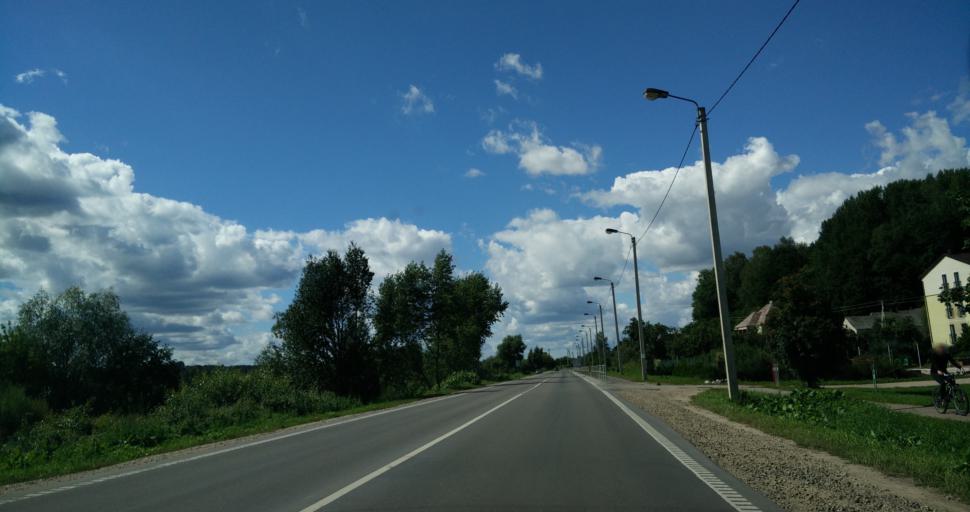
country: LT
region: Kauno apskritis
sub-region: Kauno rajonas
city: Akademija (Kaunas)
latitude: 54.9210
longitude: 23.8014
